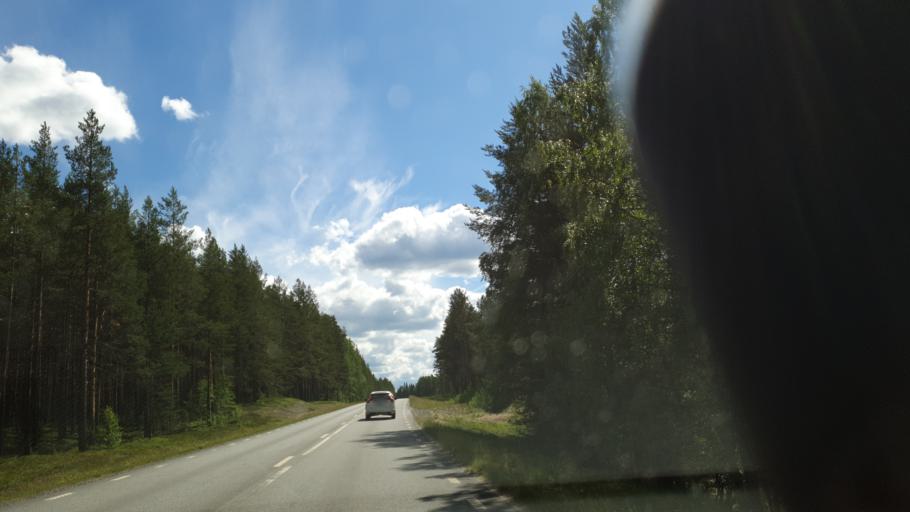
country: SE
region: Vaesterbotten
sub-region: Lycksele Kommun
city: Lycksele
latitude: 64.5695
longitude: 18.7174
